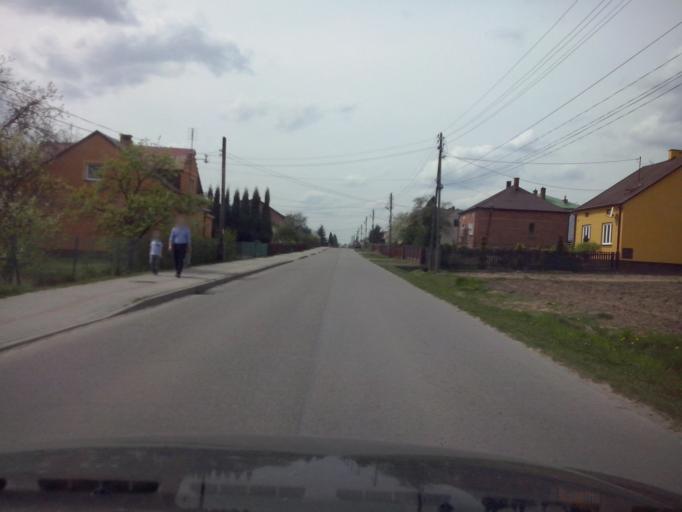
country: PL
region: Subcarpathian Voivodeship
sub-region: Powiat rzeszowski
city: Kamien
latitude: 50.3296
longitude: 22.1494
